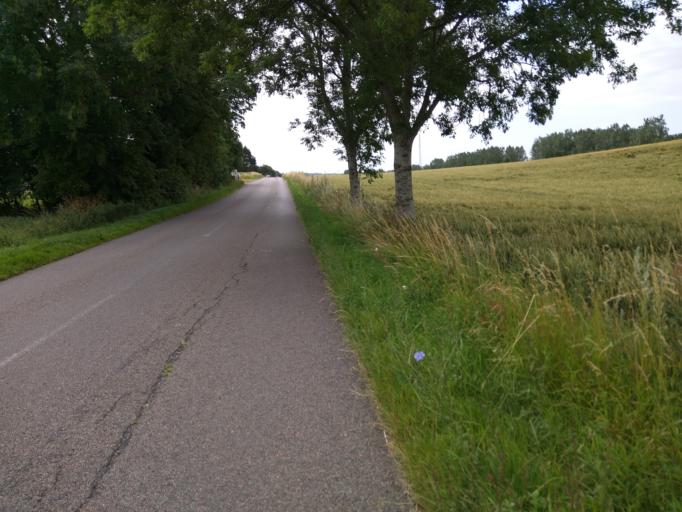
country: DK
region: Zealand
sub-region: Kalundborg Kommune
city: Svebolle
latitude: 55.7054
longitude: 11.3037
